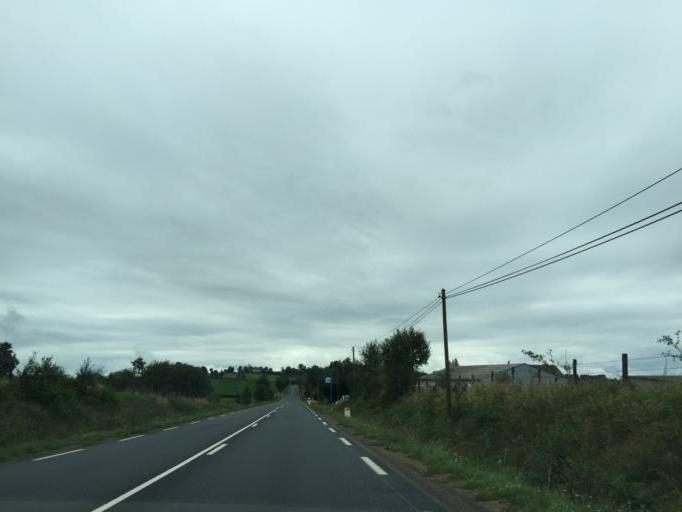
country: FR
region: Midi-Pyrenees
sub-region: Departement de l'Aveyron
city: Espalion
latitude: 44.5994
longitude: 2.7960
